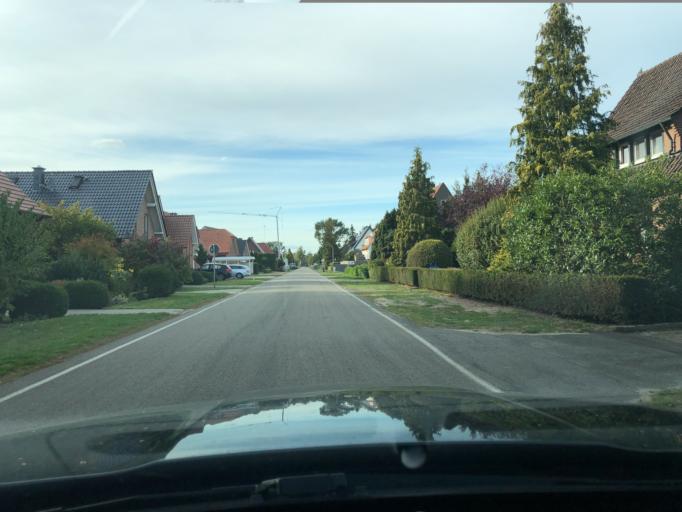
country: DE
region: North Rhine-Westphalia
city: Lengerich
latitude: 52.1659
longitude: 7.8356
